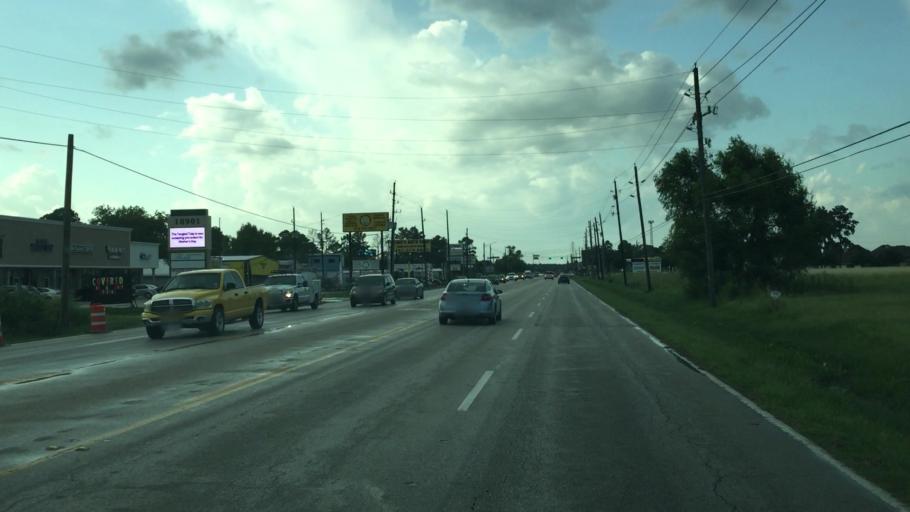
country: US
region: Texas
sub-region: Harris County
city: Spring
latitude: 30.0438
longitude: -95.4900
